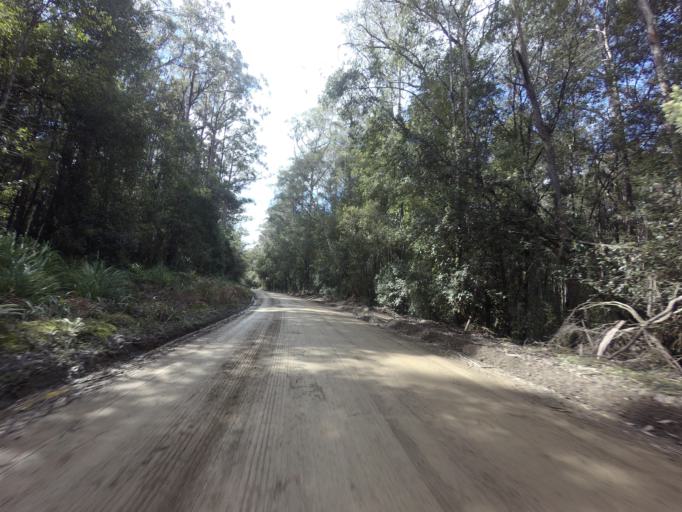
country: AU
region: Tasmania
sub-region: Huon Valley
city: Geeveston
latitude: -43.4161
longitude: 146.8886
